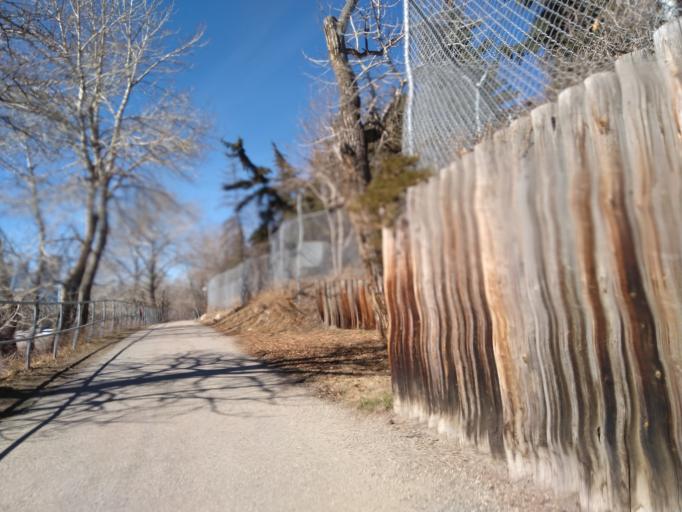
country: CA
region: Alberta
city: Calgary
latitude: 51.0469
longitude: -114.0318
